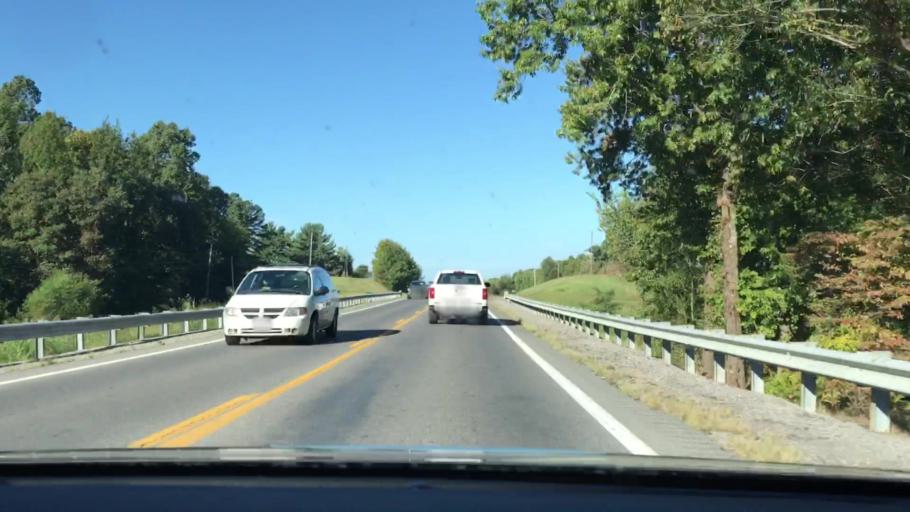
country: US
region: Kentucky
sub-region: Marshall County
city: Calvert City
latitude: 37.0048
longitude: -88.3816
